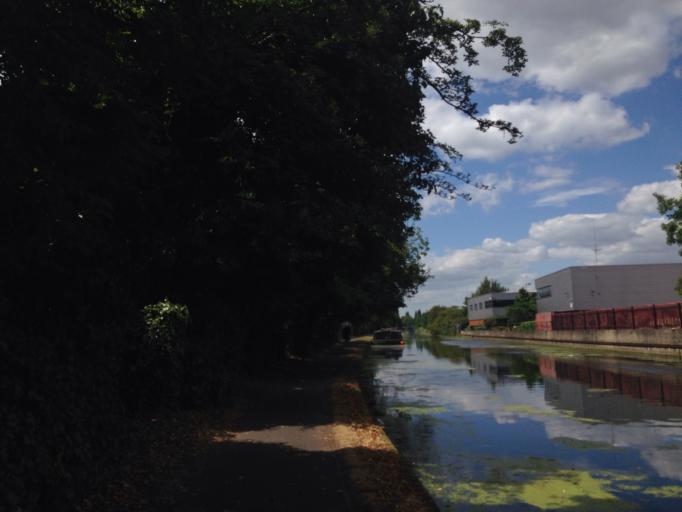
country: GB
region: England
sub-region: Greater London
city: Wembley
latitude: 51.5352
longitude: -0.2778
